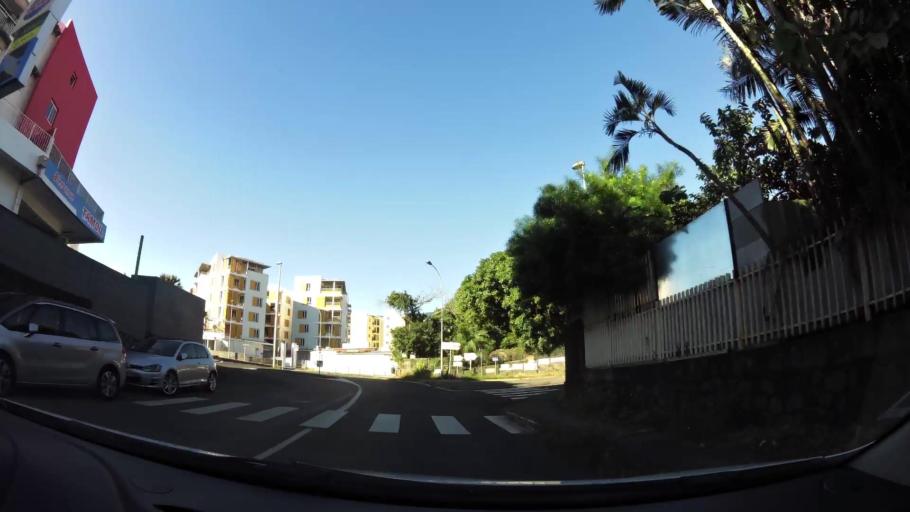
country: RE
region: Reunion
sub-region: Reunion
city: Saint-Denis
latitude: -20.8989
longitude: 55.4752
